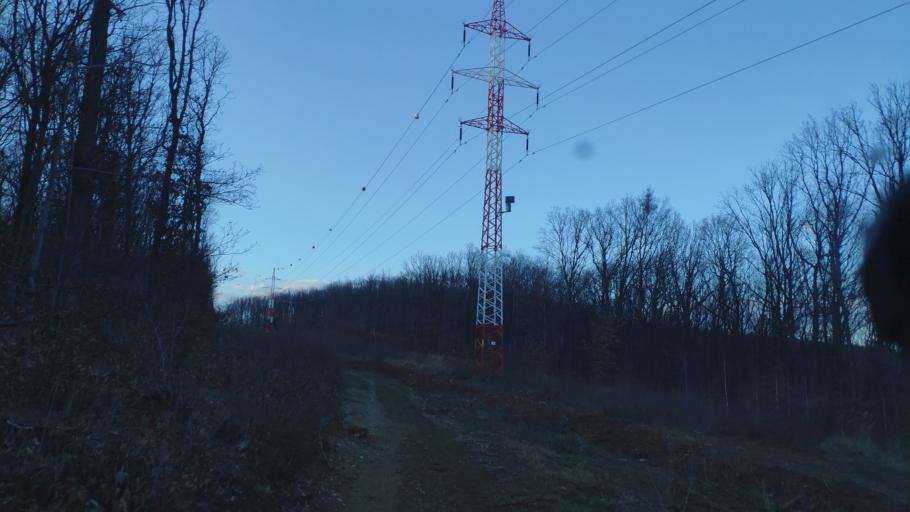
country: SK
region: Kosicky
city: Kosice
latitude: 48.6933
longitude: 21.1817
